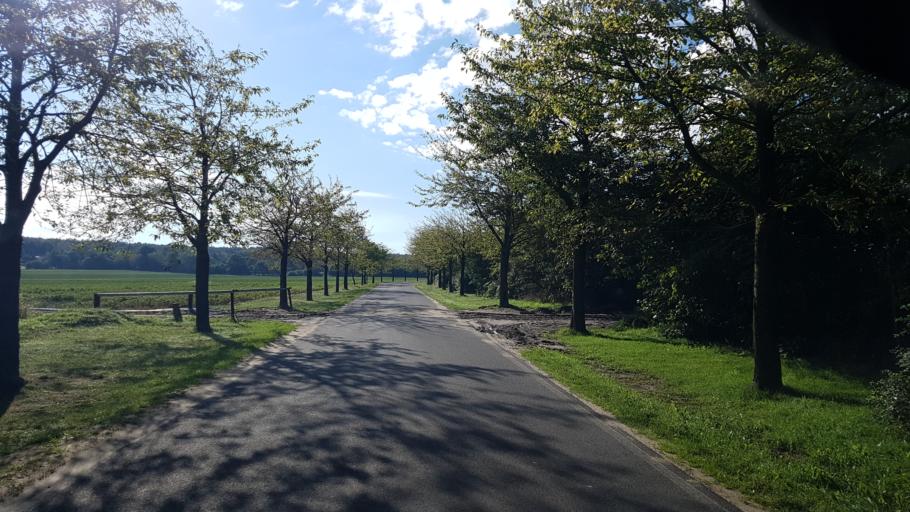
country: DE
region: Saxony
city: Gross Duben
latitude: 51.6273
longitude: 14.5316
